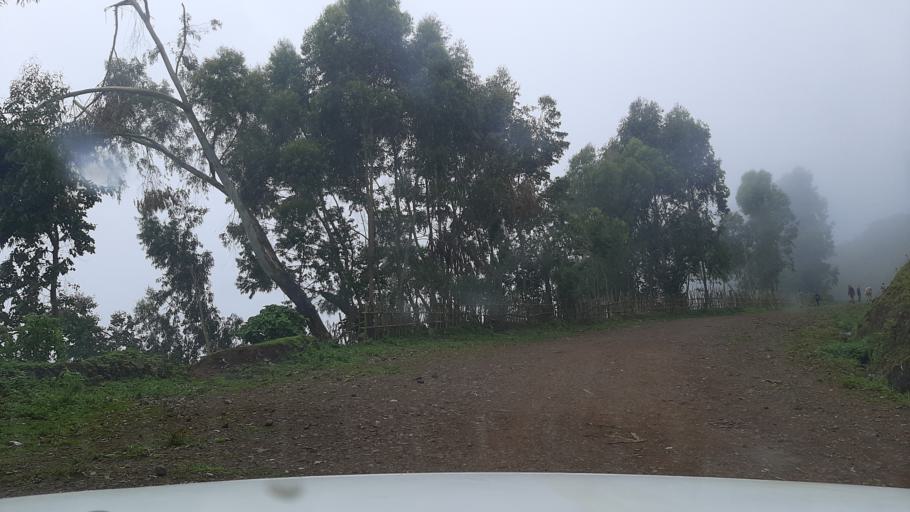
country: ET
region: Southern Nations, Nationalities, and People's Region
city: Bonga
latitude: 7.1105
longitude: 36.5646
